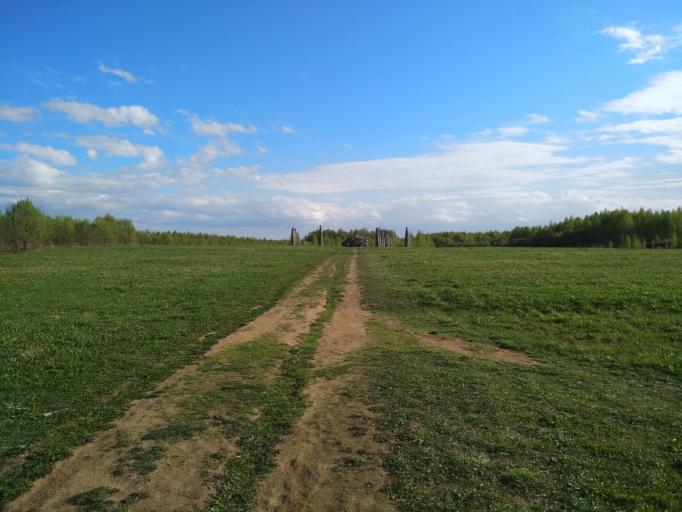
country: RU
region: Kaluga
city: Nikola-Lenivets
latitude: 54.7528
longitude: 35.6082
